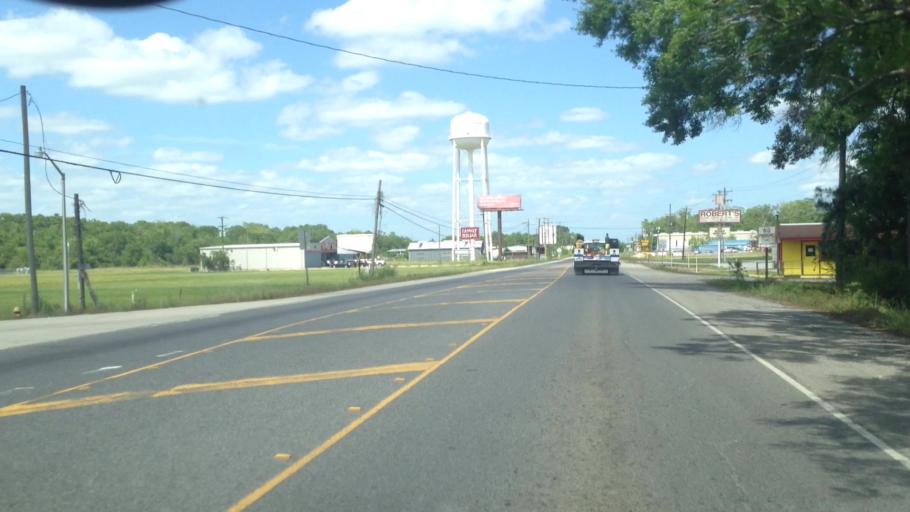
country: US
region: Louisiana
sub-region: Terrebonne Parish
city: Houma
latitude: 29.6462
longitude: -90.6869
